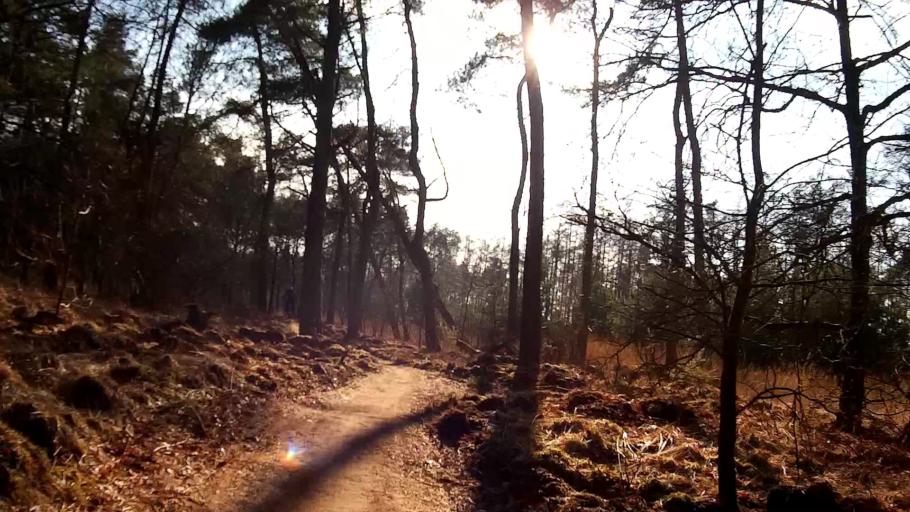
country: NL
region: Utrecht
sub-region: Gemeente Utrechtse Heuvelrug
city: Leersum
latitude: 52.0300
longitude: 5.4343
